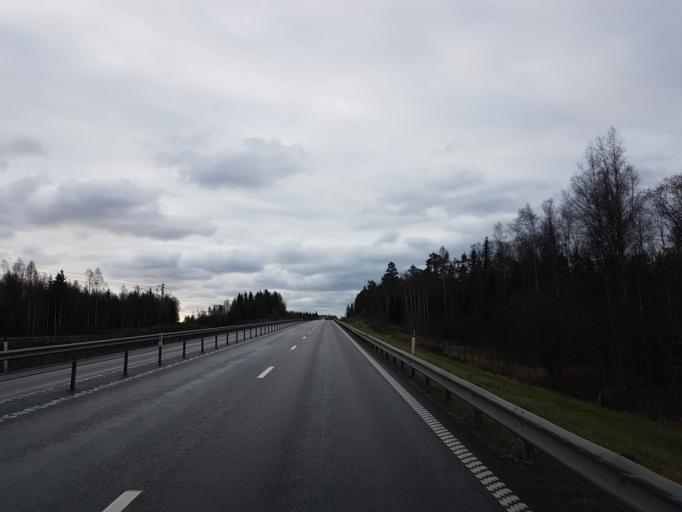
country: SE
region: Vaesternorrland
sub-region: Sundsvalls Kommun
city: Njurundabommen
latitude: 62.2179
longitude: 17.3725
